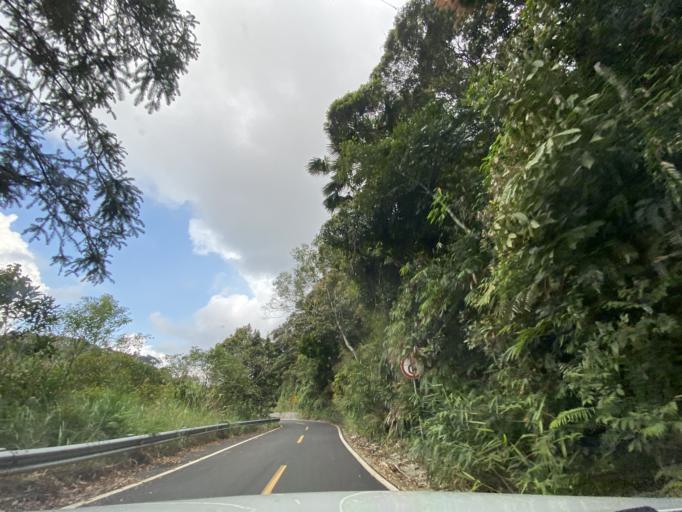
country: CN
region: Hainan
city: Diaoluoshan
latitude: 18.7165
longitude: 109.8799
